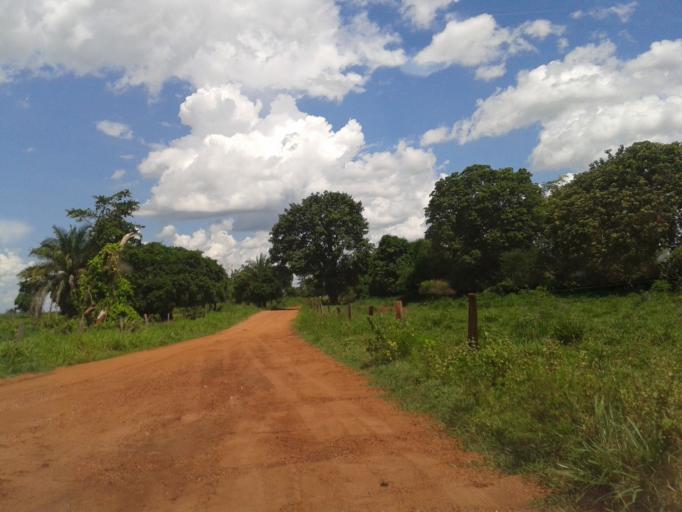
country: BR
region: Minas Gerais
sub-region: Santa Vitoria
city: Santa Vitoria
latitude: -19.1481
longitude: -50.6170
